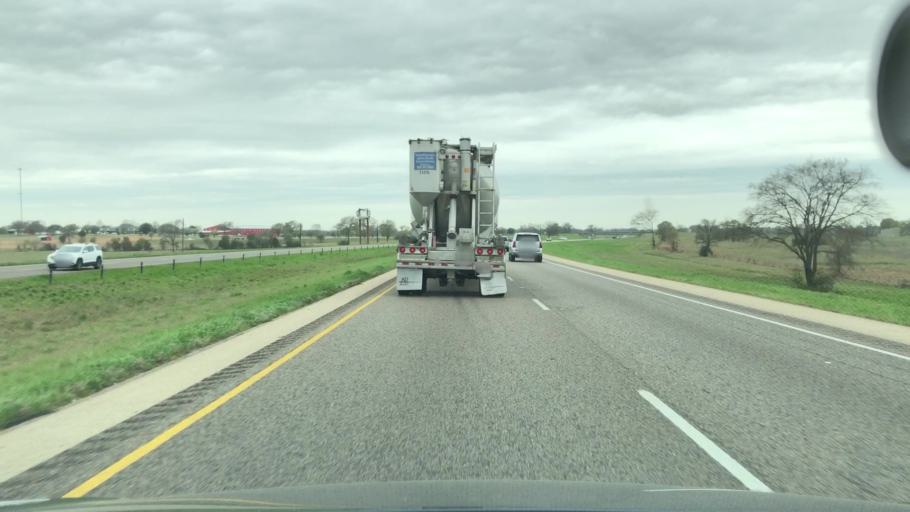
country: US
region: Texas
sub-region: Madison County
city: Madisonville
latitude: 31.0407
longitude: -95.9424
